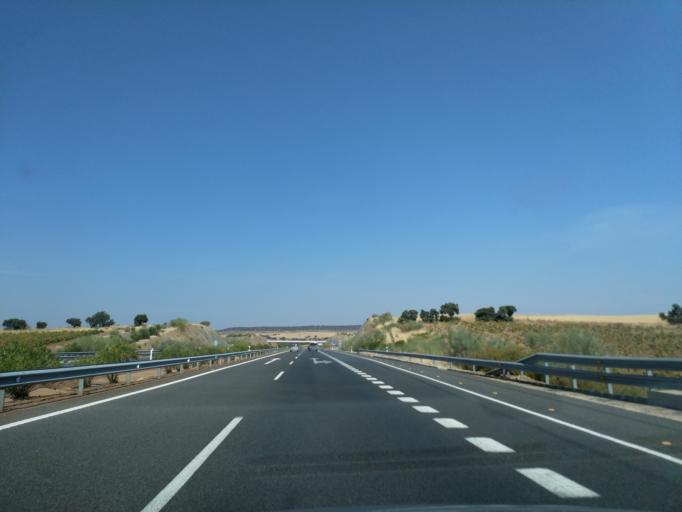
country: ES
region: Extremadura
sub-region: Provincia de Badajoz
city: Aljucen
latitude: 39.0344
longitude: -6.3364
